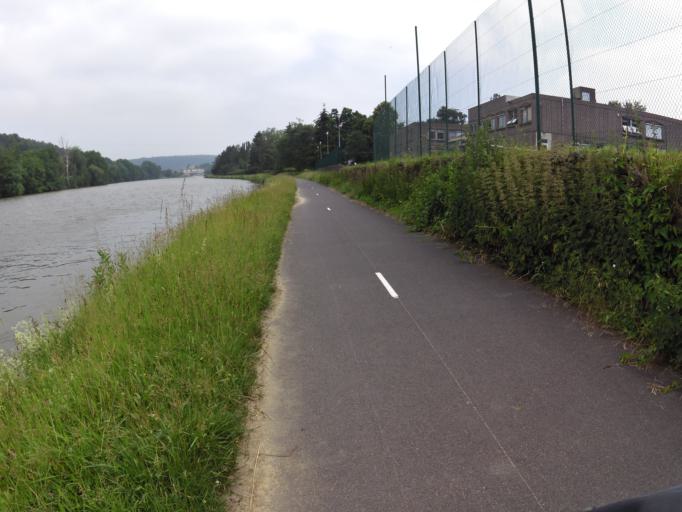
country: FR
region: Champagne-Ardenne
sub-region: Departement des Ardennes
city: Vireux-Wallerand
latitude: 50.0878
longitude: 4.7278
